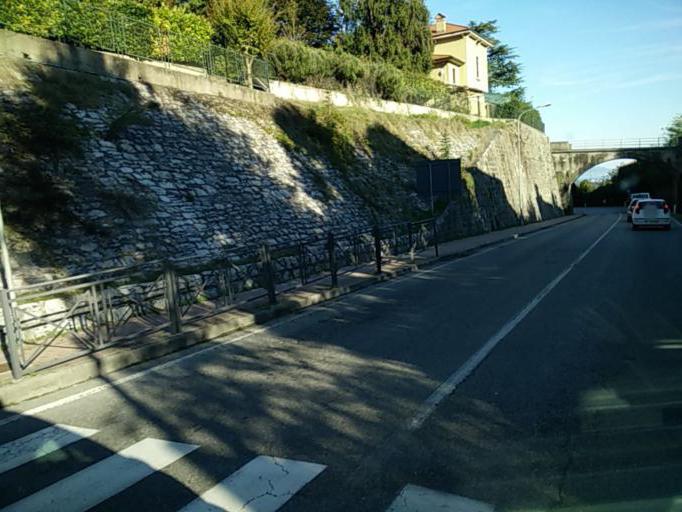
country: IT
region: Lombardy
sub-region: Provincia di Brescia
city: Roe Volciano
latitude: 45.6115
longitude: 10.4818
